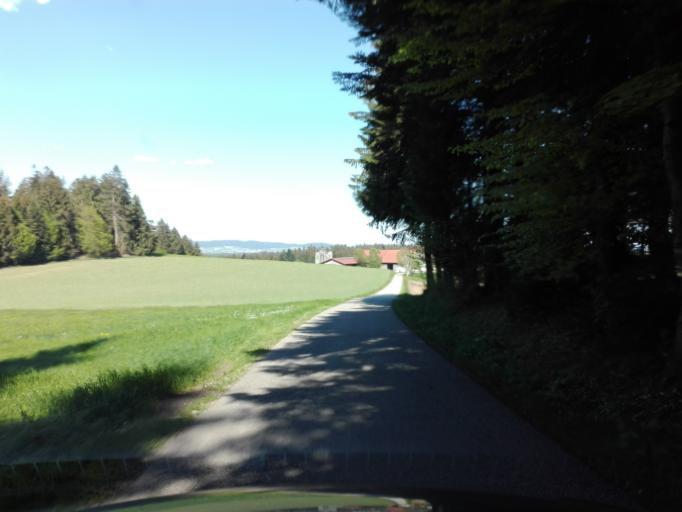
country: DE
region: Bavaria
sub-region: Lower Bavaria
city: Obernzell
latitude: 48.4387
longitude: 13.6990
